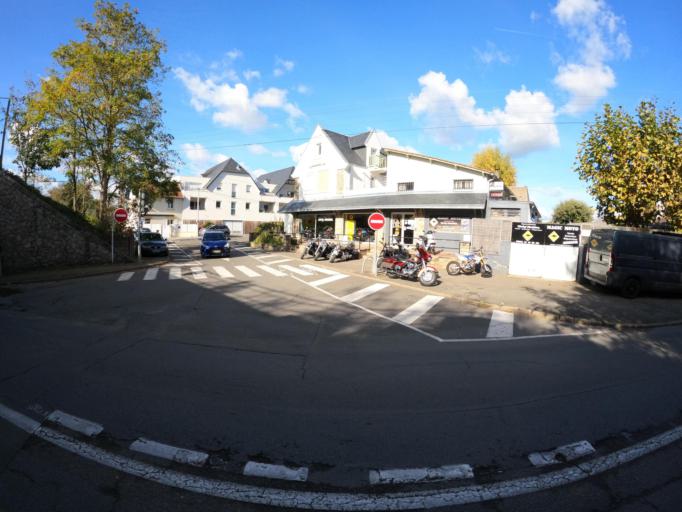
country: FR
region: Pays de la Loire
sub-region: Departement de la Loire-Atlantique
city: La Baule-Escoublac
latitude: 47.2885
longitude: -2.3762
